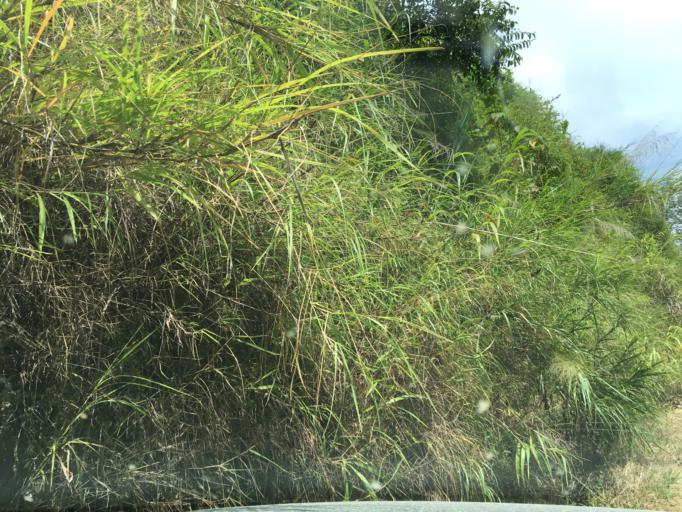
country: CN
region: Guangxi Zhuangzu Zizhiqu
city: Xinzhou
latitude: 24.9533
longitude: 105.7894
